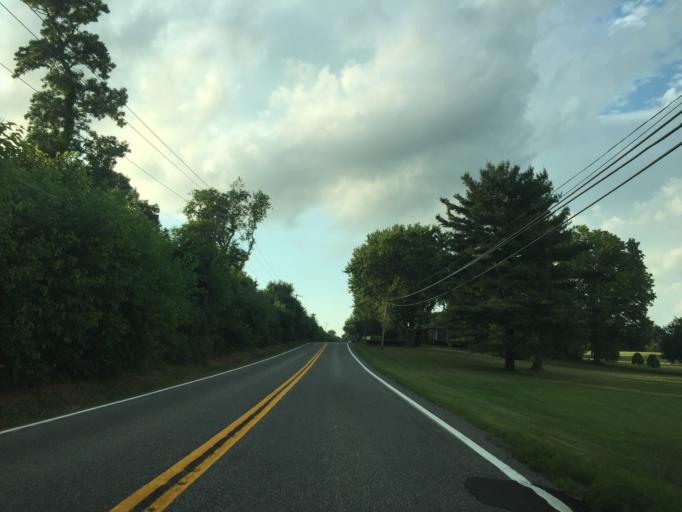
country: US
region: Maryland
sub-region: Harford County
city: Jarrettsville
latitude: 39.5646
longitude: -76.4985
